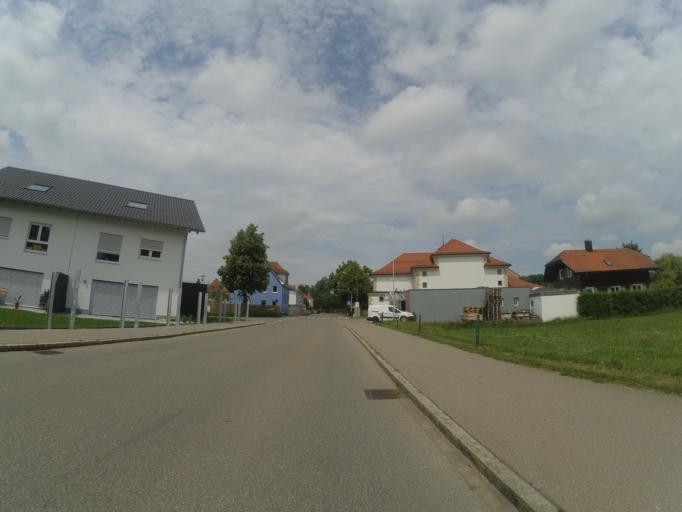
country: DE
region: Baden-Wuerttemberg
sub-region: Tuebingen Region
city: Leutkirch im Allgau
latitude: 47.8215
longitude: 10.0204
